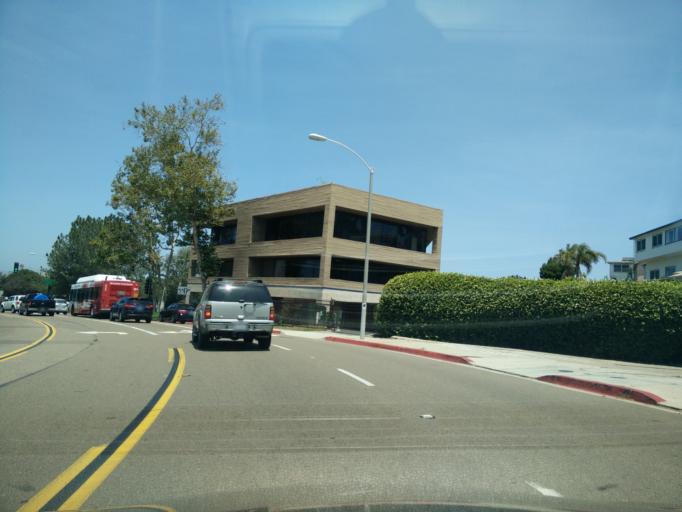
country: US
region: California
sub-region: San Diego County
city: San Diego
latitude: 32.7722
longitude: -117.2021
